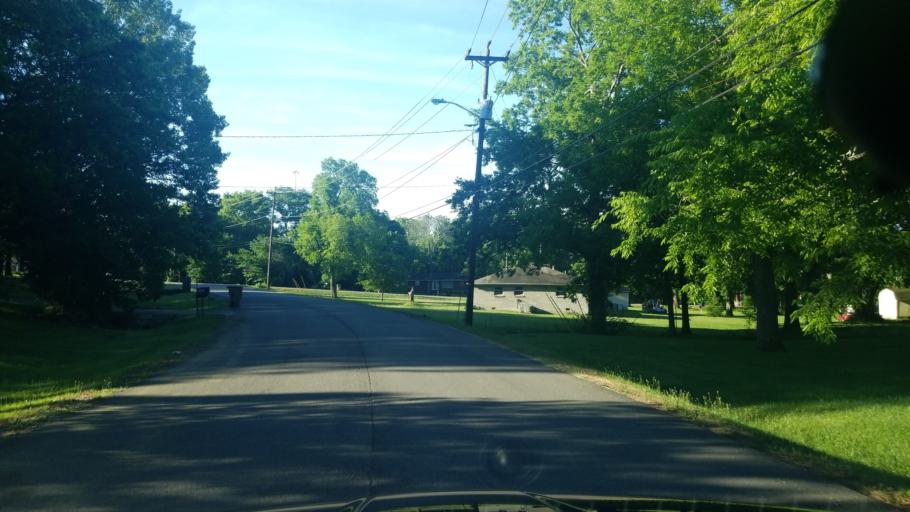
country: US
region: Tennessee
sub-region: Davidson County
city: Nashville
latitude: 36.2388
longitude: -86.7631
